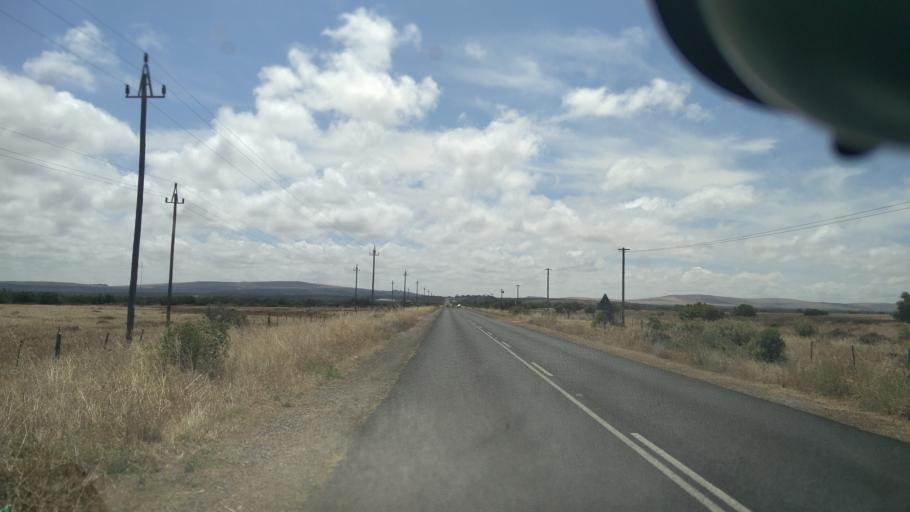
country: ZA
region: Western Cape
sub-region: City of Cape Town
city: Atlantis
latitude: -33.3417
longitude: 18.1787
